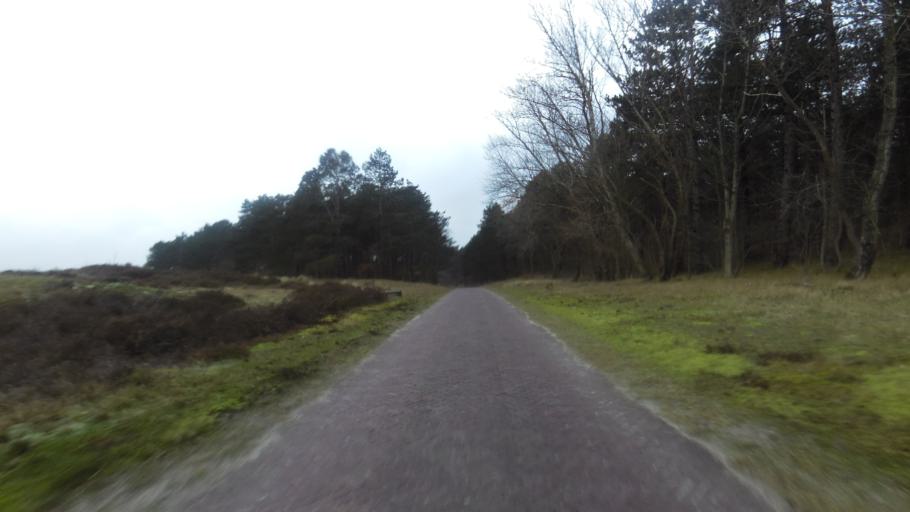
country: NL
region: North Holland
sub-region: Gemeente Bergen
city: Egmond aan Zee
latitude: 52.6739
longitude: 4.6578
